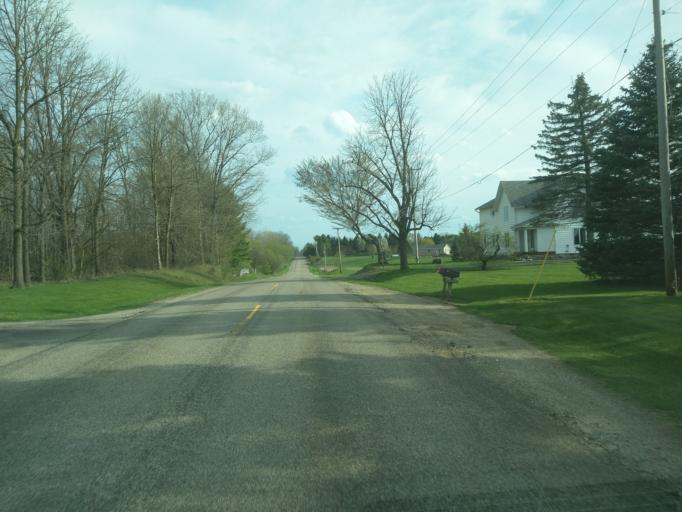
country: US
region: Michigan
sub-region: Eaton County
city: Dimondale
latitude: 42.6309
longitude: -84.6421
